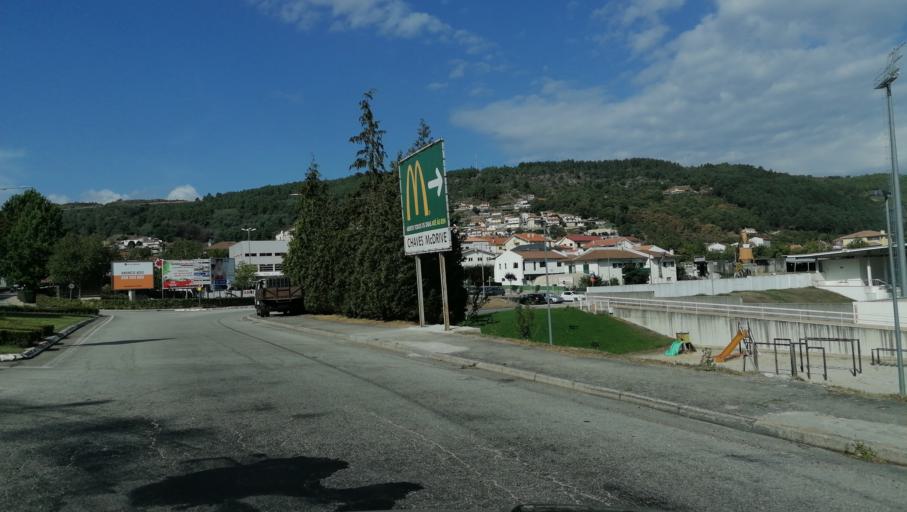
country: PT
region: Vila Real
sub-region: Vila Pouca de Aguiar
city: Vila Pouca de Aguiar
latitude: 41.5020
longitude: -7.6395
